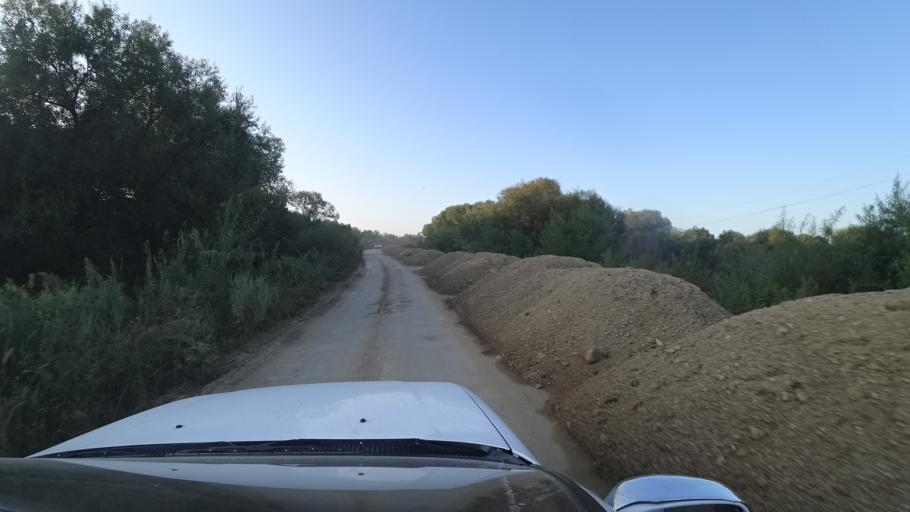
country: RU
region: Primorskiy
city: Dal'nerechensk
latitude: 45.9373
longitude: 133.7602
